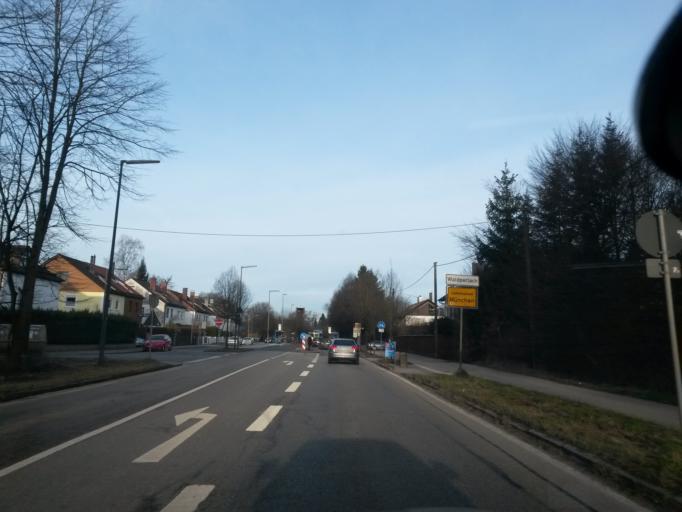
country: DE
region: Bavaria
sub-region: Upper Bavaria
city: Neubiberg
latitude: 48.0831
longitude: 11.6817
